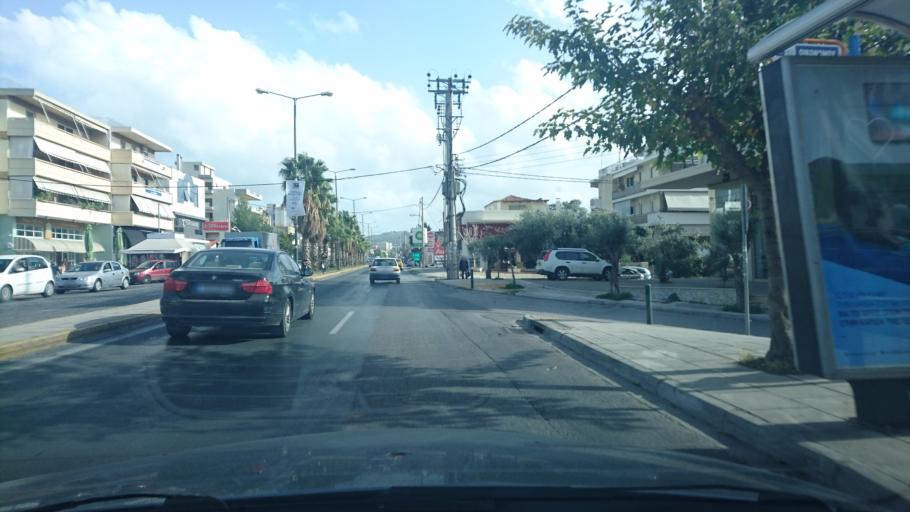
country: GR
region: Attica
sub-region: Nomarchia Athinas
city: Khalandrion
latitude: 38.0186
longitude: 23.8081
